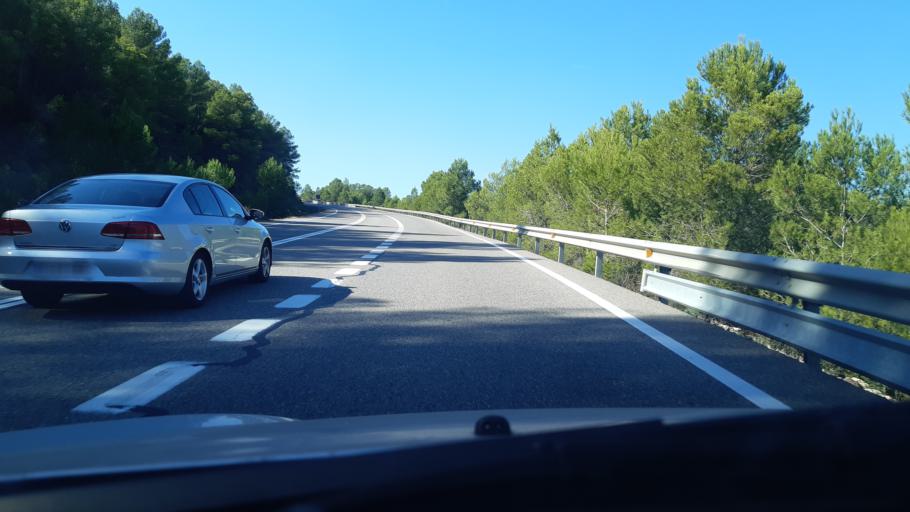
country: ES
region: Catalonia
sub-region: Provincia de Tarragona
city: Rasquera
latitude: 40.9943
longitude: 0.5575
